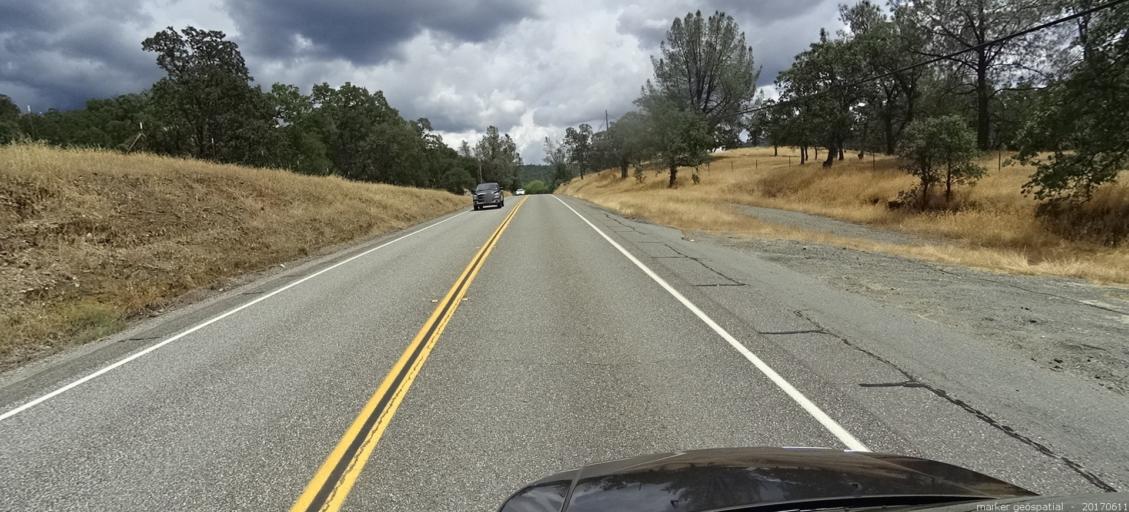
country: US
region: California
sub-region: Butte County
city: Paradise
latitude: 39.6566
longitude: -121.5721
